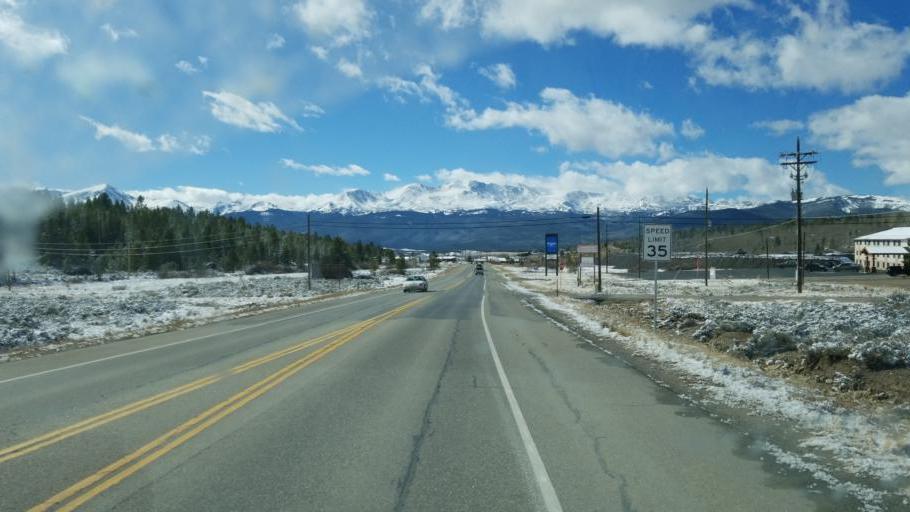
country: US
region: Colorado
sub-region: Lake County
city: Leadville
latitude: 39.2394
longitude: -106.3052
